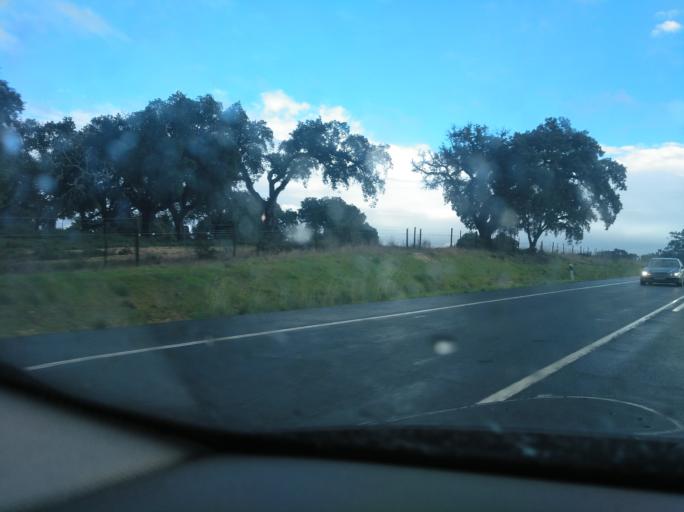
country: PT
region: Setubal
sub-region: Grandola
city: Grandola
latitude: 38.0195
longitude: -8.3983
